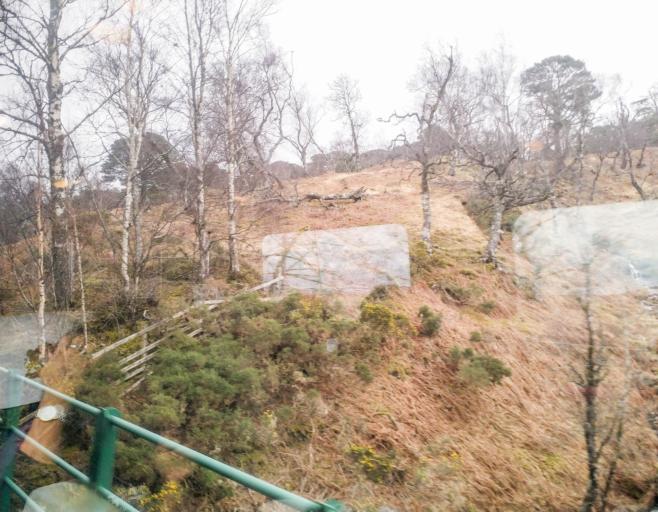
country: GB
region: Scotland
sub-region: Highland
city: Spean Bridge
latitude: 56.5749
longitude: -4.6847
